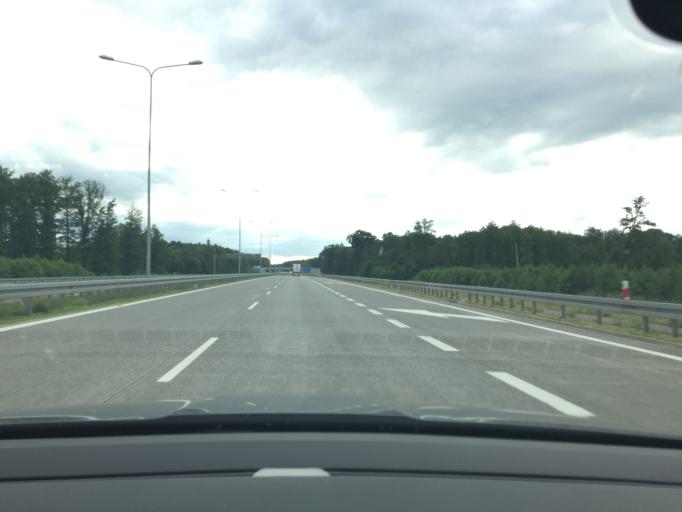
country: PL
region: Lubusz
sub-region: Powiat miedzyrzecki
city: Trzciel
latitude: 52.3290
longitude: 15.8656
